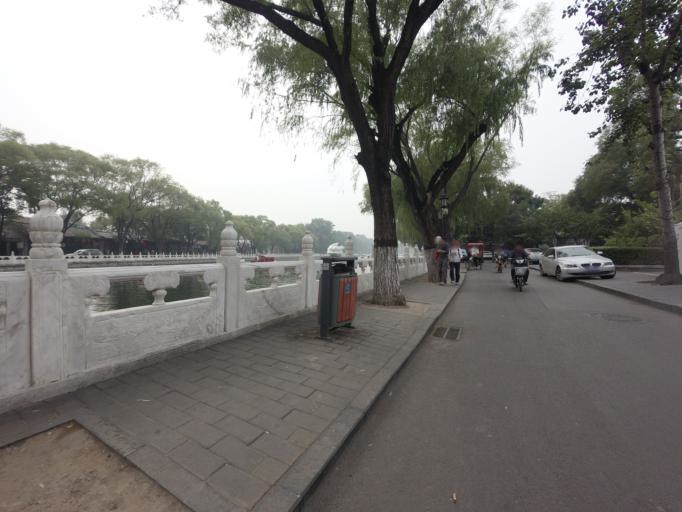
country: CN
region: Beijing
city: Jingshan
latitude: 39.9381
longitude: 116.3863
